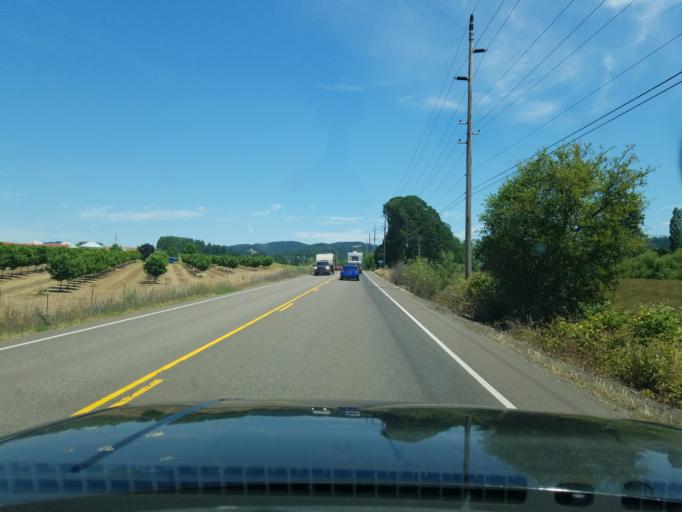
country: US
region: Oregon
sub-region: Yamhill County
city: Yamhill
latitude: 45.3548
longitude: -123.1708
